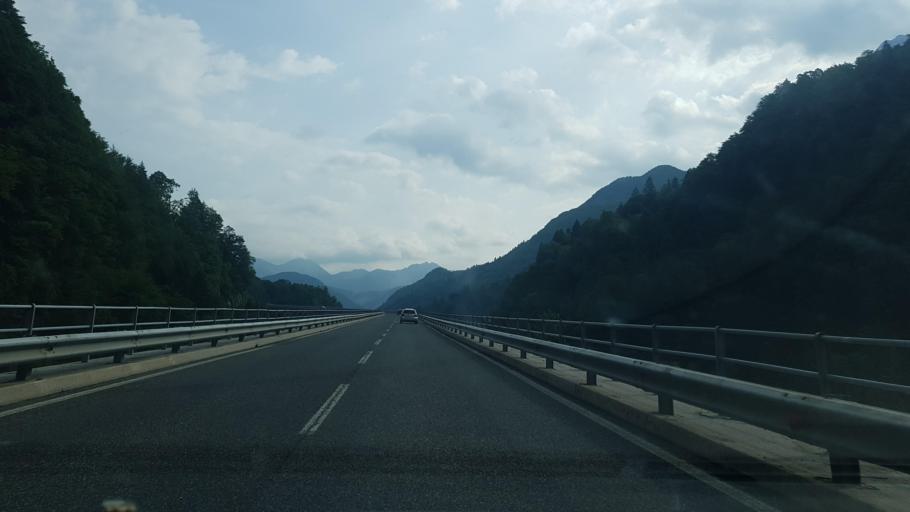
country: IT
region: Friuli Venezia Giulia
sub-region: Provincia di Udine
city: Paularo
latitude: 46.4817
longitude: 13.0902
